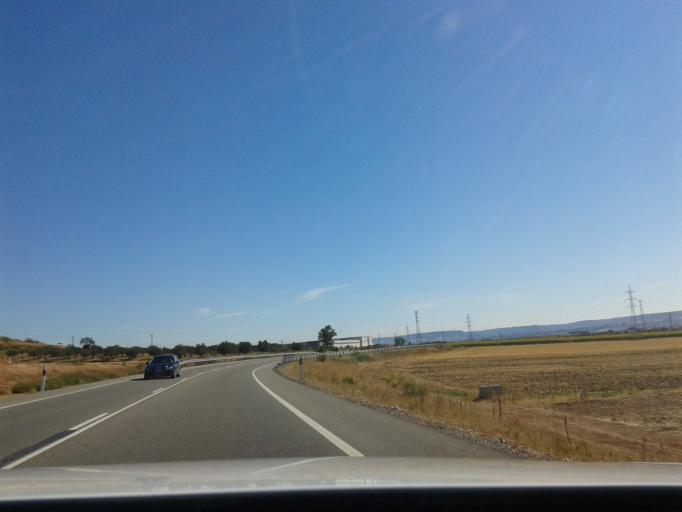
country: ES
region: Castille-La Mancha
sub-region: Provincia de Guadalajara
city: Quer
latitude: 40.5903
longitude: -3.2687
